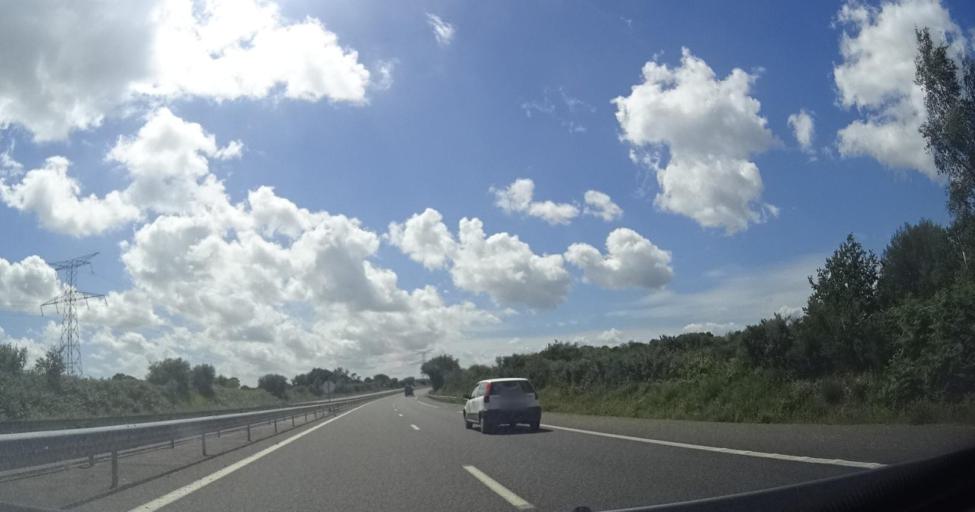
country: FR
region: Brittany
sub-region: Departement du Morbihan
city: Pluherlin
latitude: 47.6690
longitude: -2.3476
